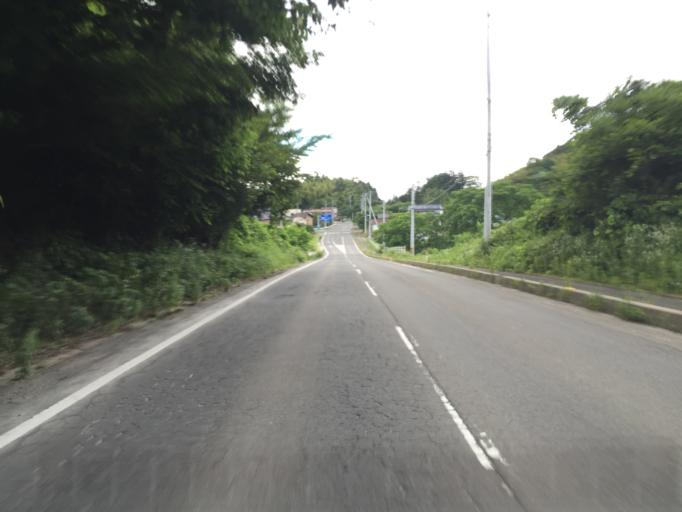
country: JP
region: Fukushima
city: Fukushima-shi
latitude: 37.6821
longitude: 140.5028
